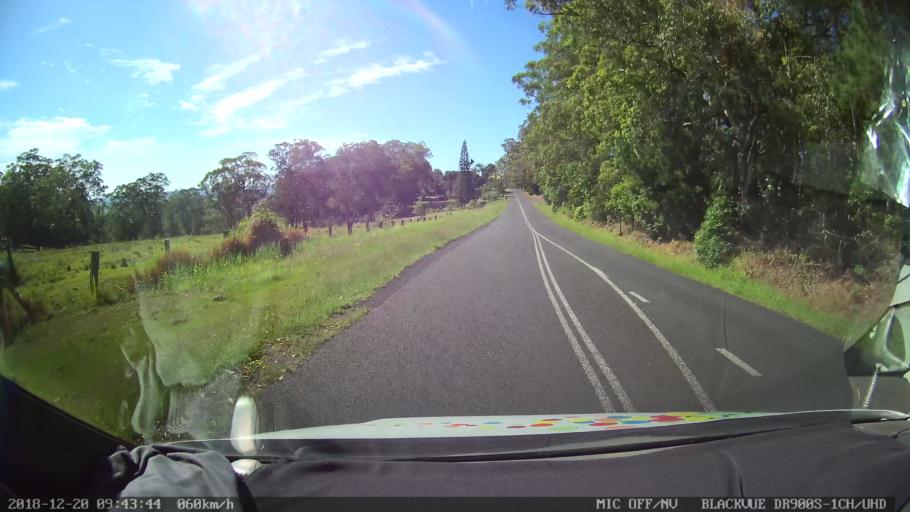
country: AU
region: New South Wales
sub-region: Lismore Municipality
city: Lismore
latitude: -28.7283
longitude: 153.2974
